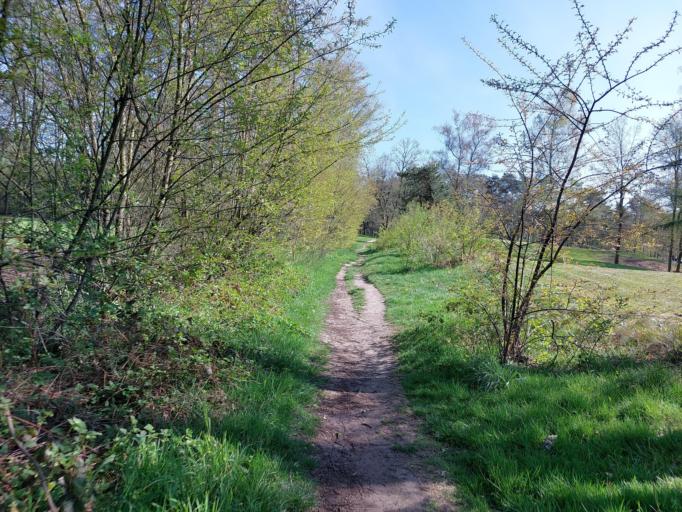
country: BE
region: Wallonia
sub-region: Province du Hainaut
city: Jurbise
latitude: 50.5060
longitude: 3.9219
